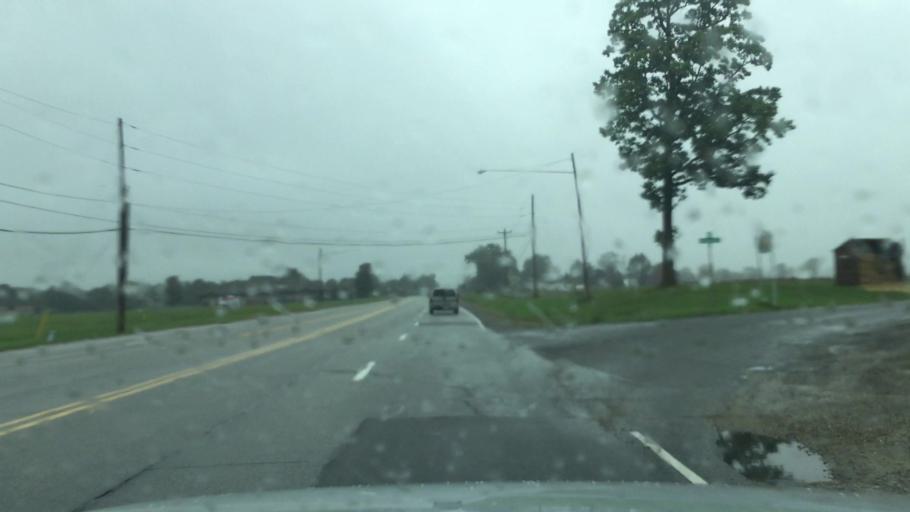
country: US
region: Michigan
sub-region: Saginaw County
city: Bridgeport
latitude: 43.3360
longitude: -83.8357
